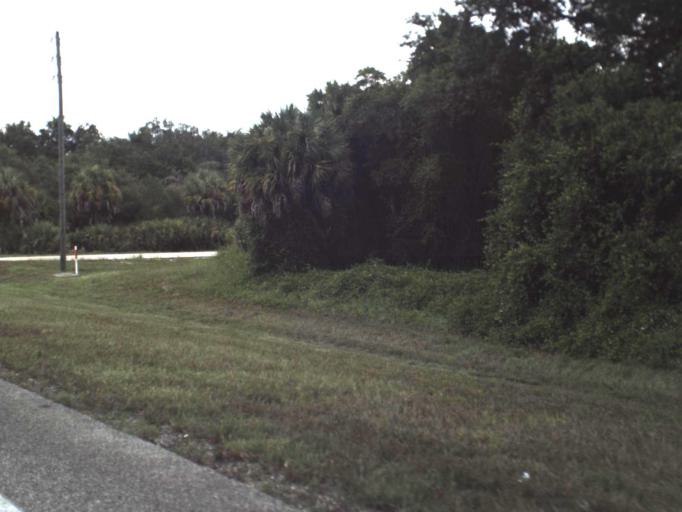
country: US
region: Florida
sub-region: Sarasota County
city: North Port
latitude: 27.0185
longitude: -82.1761
